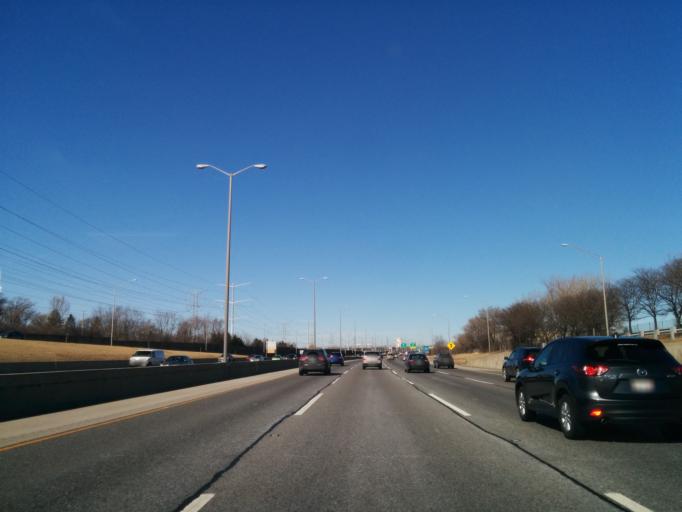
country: US
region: Illinois
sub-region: DuPage County
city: Lisle
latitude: 41.7882
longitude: -88.0562
